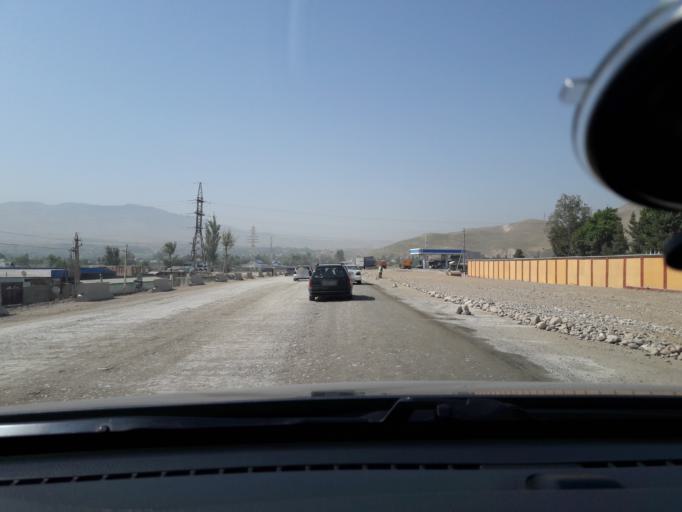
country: TJ
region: Dushanbe
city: Boshkengash
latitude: 38.4547
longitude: 68.7357
